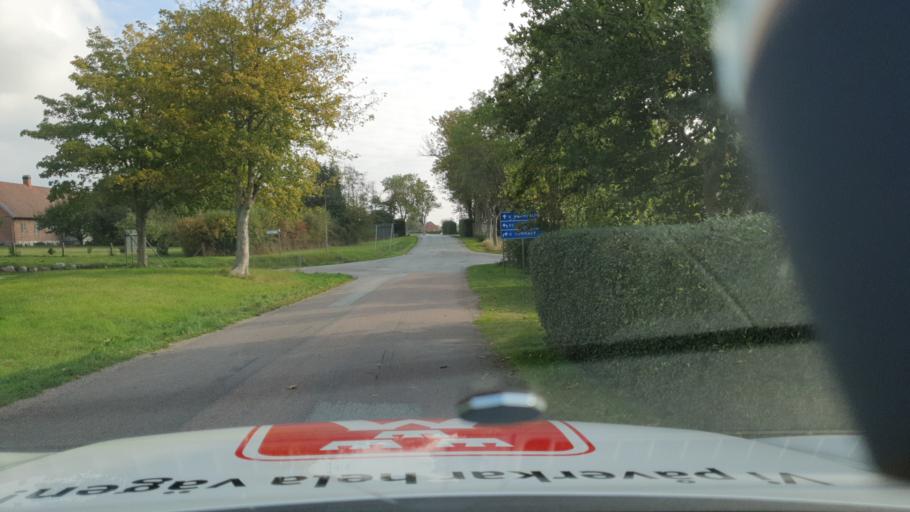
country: SE
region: Skane
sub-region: Trelleborgs Kommun
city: Trelleborg
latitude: 55.4144
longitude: 13.1342
